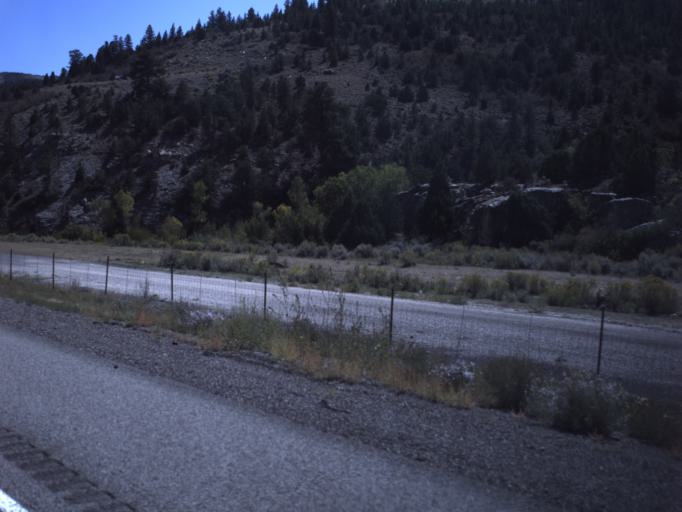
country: US
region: Utah
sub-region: Wayne County
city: Loa
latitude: 38.7603
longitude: -111.4544
